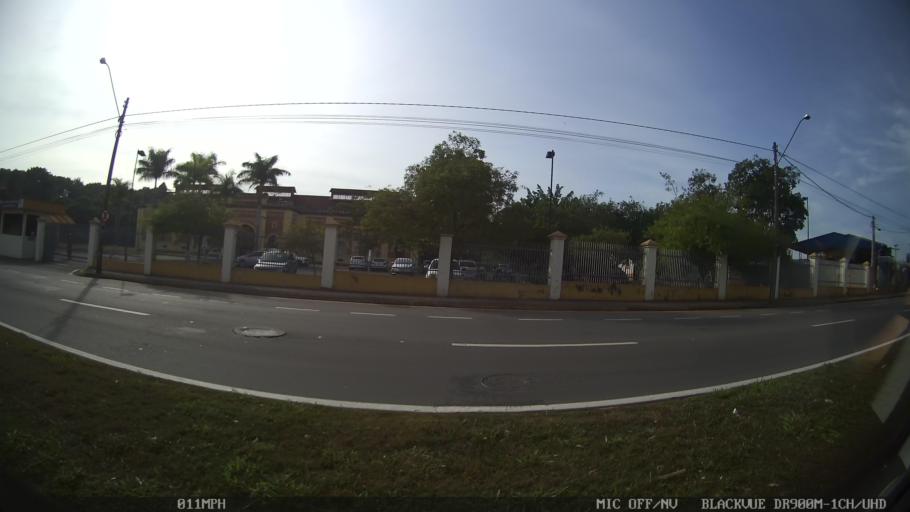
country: BR
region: Sao Paulo
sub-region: Piracicaba
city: Piracicaba
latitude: -22.6913
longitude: -47.6732
